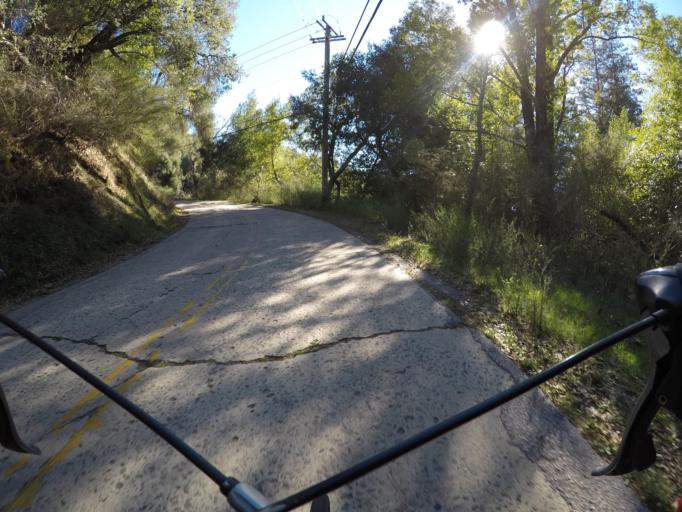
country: US
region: California
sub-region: Santa Clara County
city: Lexington Hills
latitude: 37.1249
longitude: -121.9832
